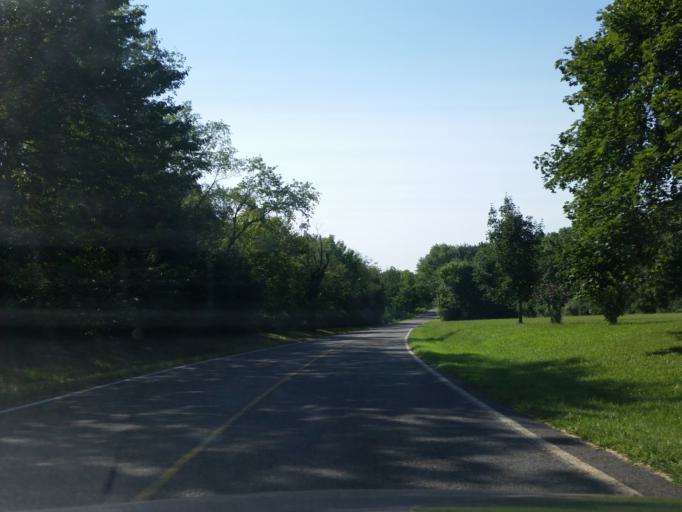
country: US
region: Pennsylvania
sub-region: Lebanon County
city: Jonestown
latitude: 40.4691
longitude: -76.5199
